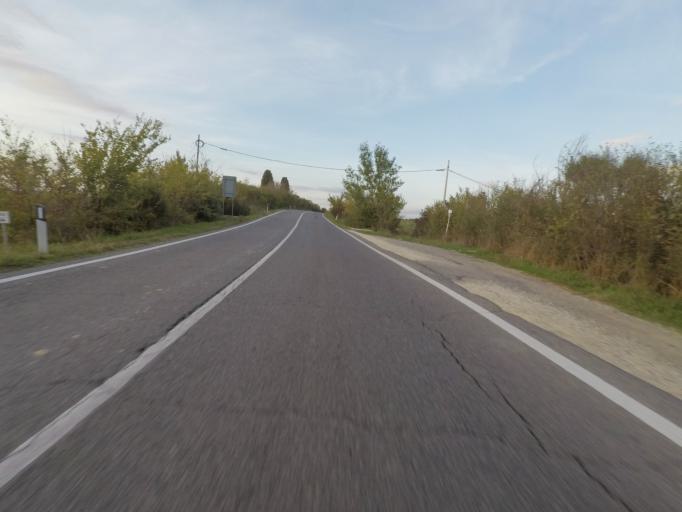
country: IT
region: Tuscany
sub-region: Provincia di Siena
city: Pienza
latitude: 43.0936
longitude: 11.6890
